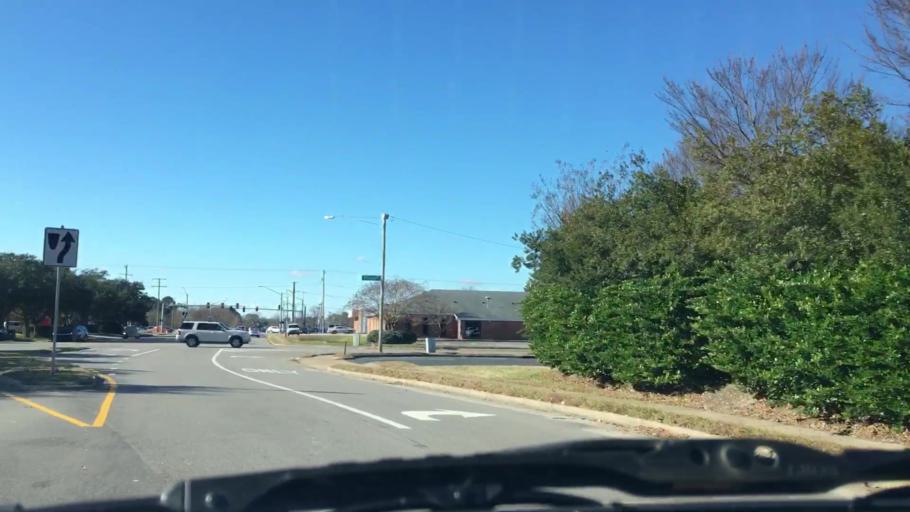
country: US
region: Virginia
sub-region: City of Virginia Beach
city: Virginia Beach
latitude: 36.8491
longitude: -76.0191
